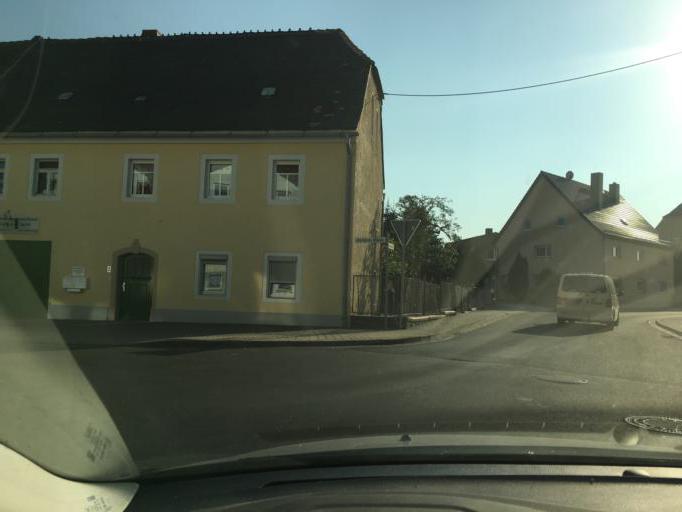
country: DE
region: Saxony
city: Wermsdorf
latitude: 51.2809
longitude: 12.9421
